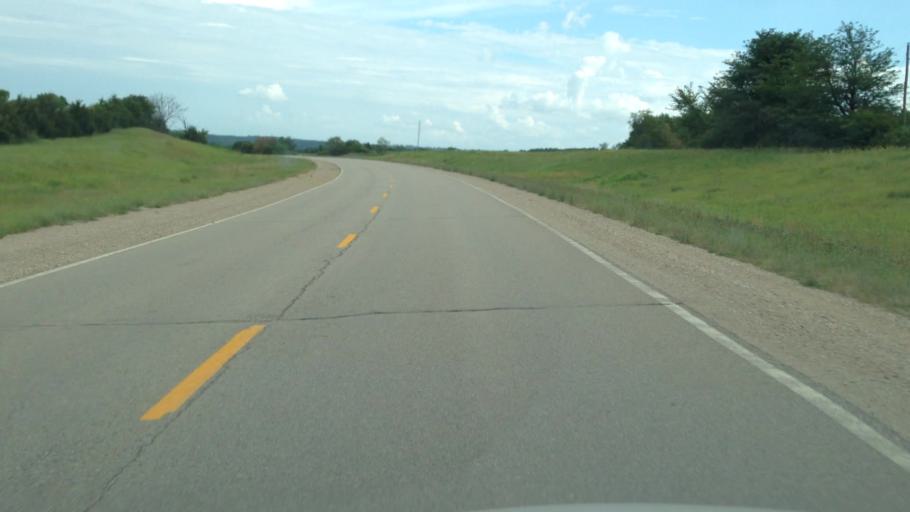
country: US
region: Kansas
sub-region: Shawnee County
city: Topeka
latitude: 39.1004
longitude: -95.4836
